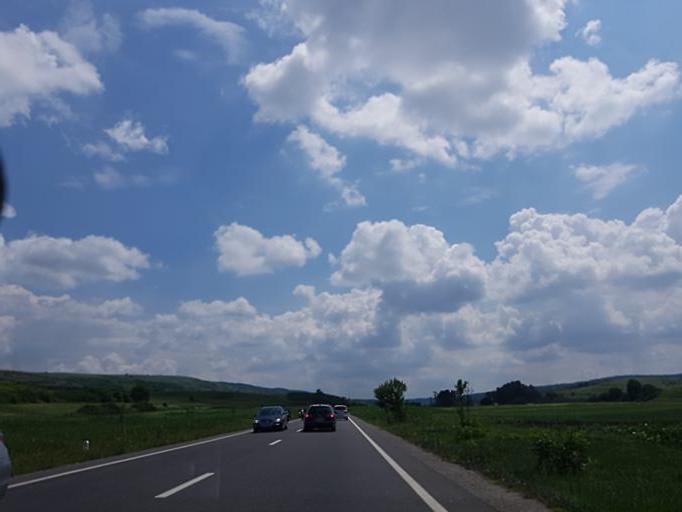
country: RO
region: Sibiu
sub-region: Comuna Seica Mare
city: Seica Mare
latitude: 45.9725
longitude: 24.1492
